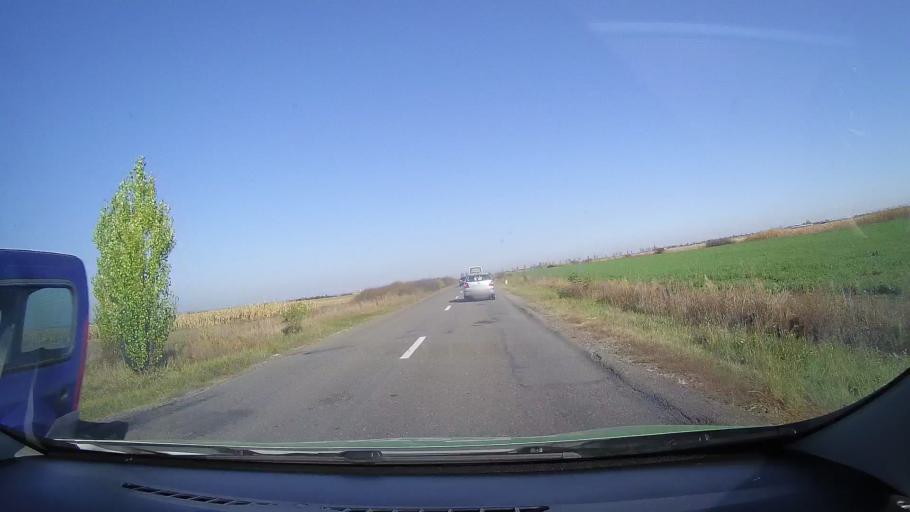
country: RO
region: Satu Mare
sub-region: Comuna Cauas
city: Cauas
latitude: 47.5837
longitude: 22.5475
